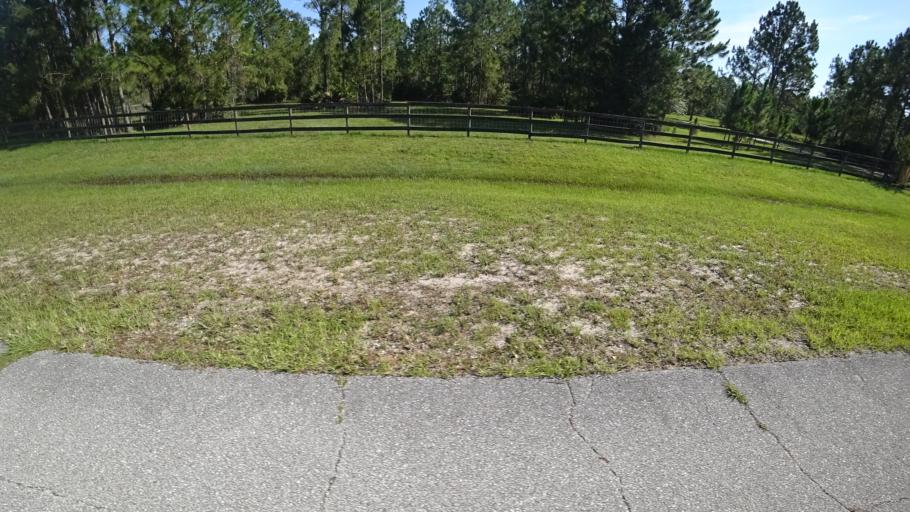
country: US
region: Florida
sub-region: Sarasota County
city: The Meadows
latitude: 27.4244
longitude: -82.3468
